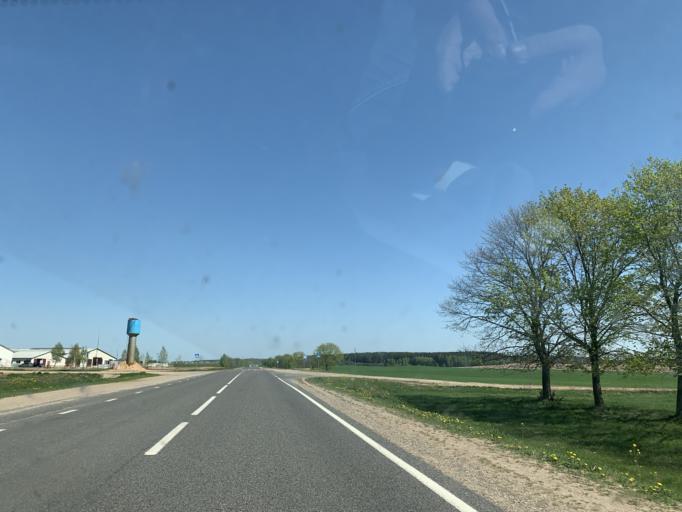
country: BY
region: Minsk
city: Tsimkavichy
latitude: 53.2524
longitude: 26.9126
